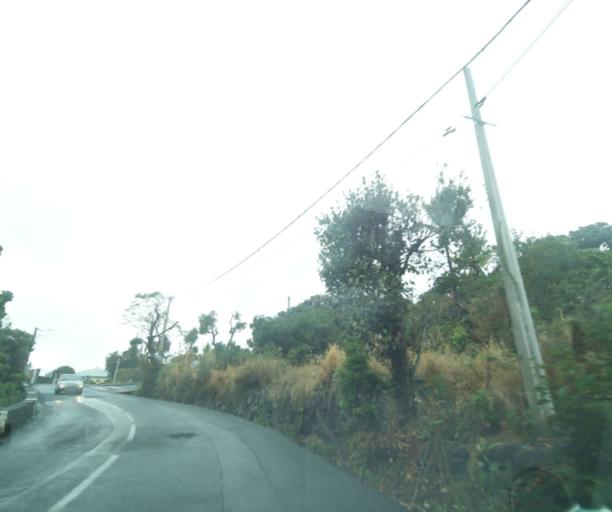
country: RE
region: Reunion
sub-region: Reunion
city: Saint-Paul
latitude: -21.0222
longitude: 55.2885
